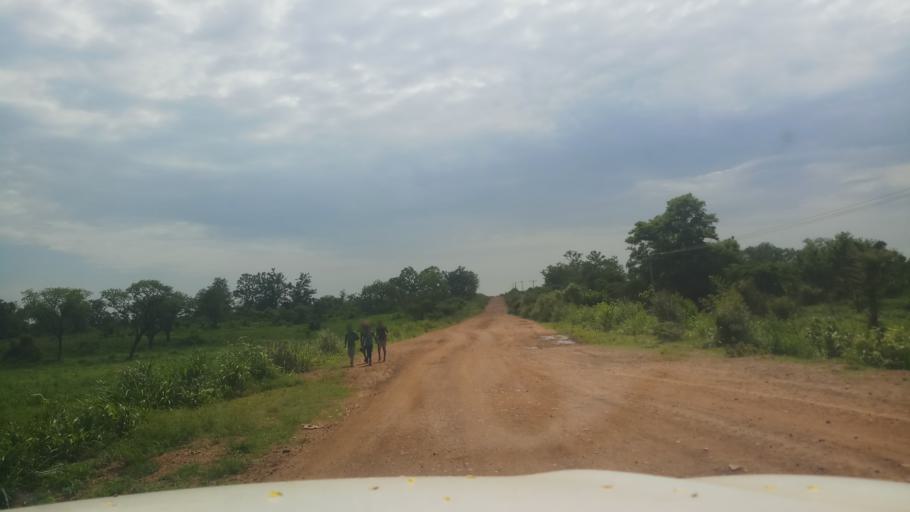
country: ET
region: Gambela
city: Gambela
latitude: 8.2139
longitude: 34.5560
